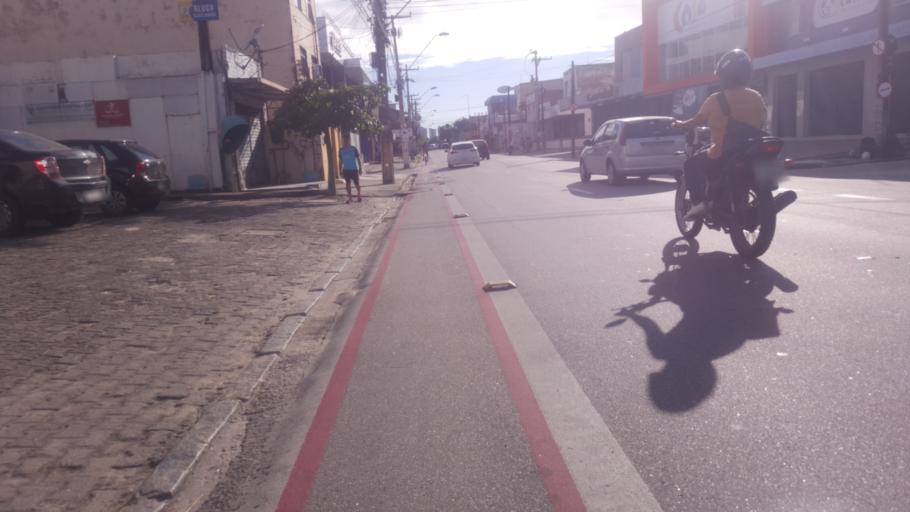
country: BR
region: Ceara
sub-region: Fortaleza
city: Fortaleza
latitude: -3.7593
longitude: -38.5441
